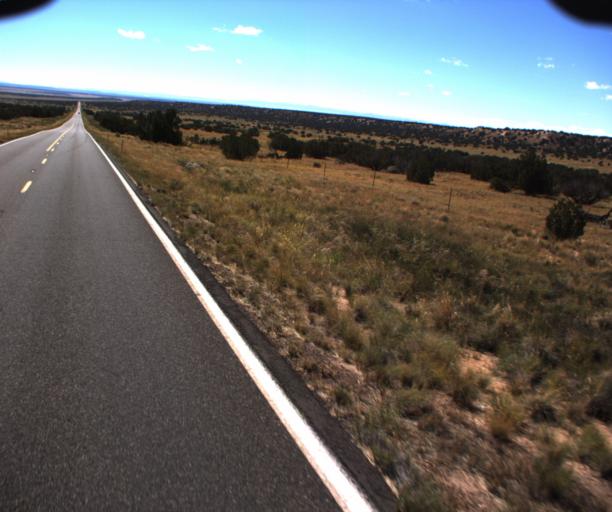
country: US
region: Arizona
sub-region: Apache County
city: Saint Johns
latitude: 34.8167
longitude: -109.2376
